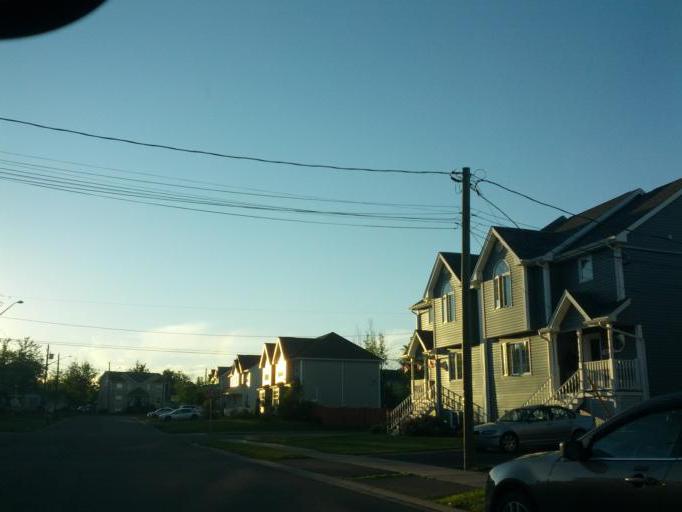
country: CA
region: New Brunswick
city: Moncton
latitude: 46.1145
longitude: -64.8565
